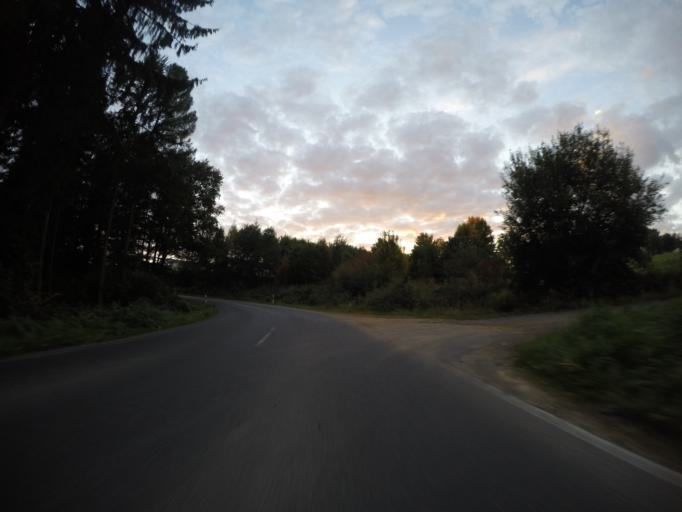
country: DE
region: Rheinland-Pfalz
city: Meinborn
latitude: 50.5059
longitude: 7.5673
